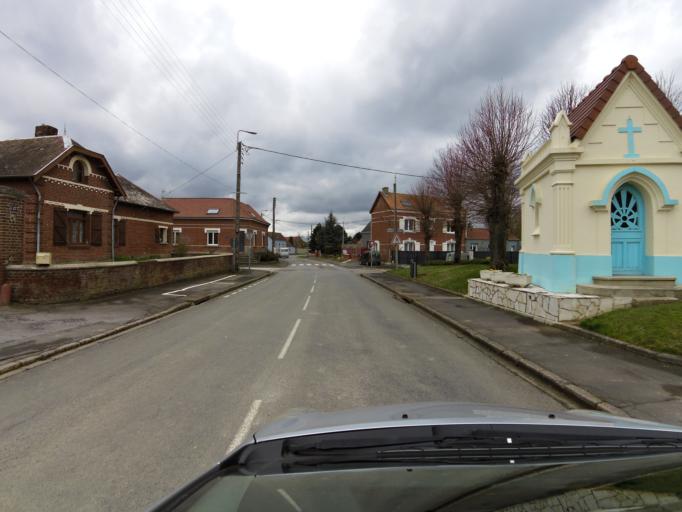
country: FR
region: Nord-Pas-de-Calais
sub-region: Departement du Pas-de-Calais
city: Beaurains
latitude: 50.2351
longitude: 2.7888
